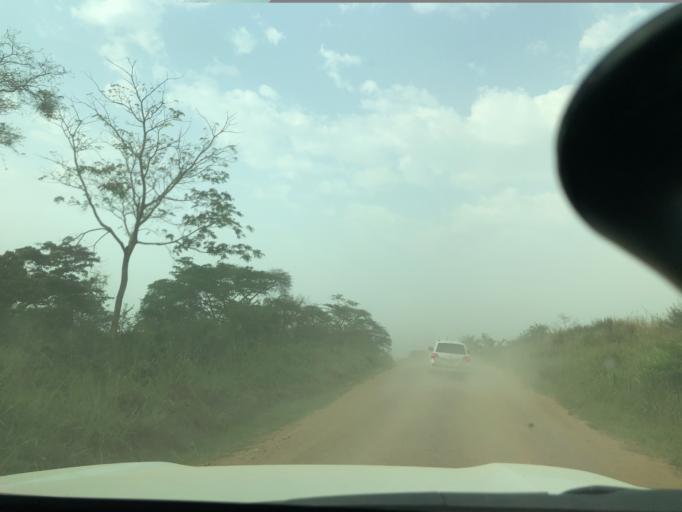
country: UG
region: Western Region
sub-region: Kasese District
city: Margherita
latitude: 0.2140
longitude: 29.6782
